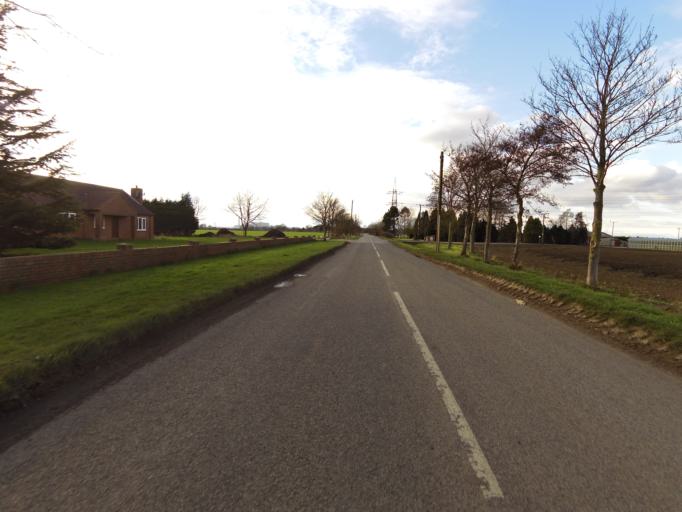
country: GB
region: England
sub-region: East Riding of Yorkshire
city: Snaith
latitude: 53.7049
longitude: -1.0403
